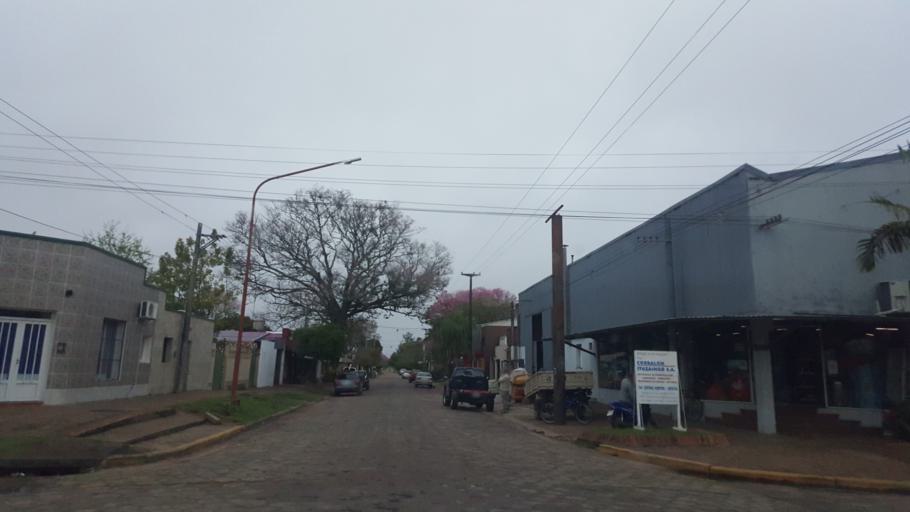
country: AR
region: Corrientes
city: Ituzaingo
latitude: -27.5885
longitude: -56.6916
